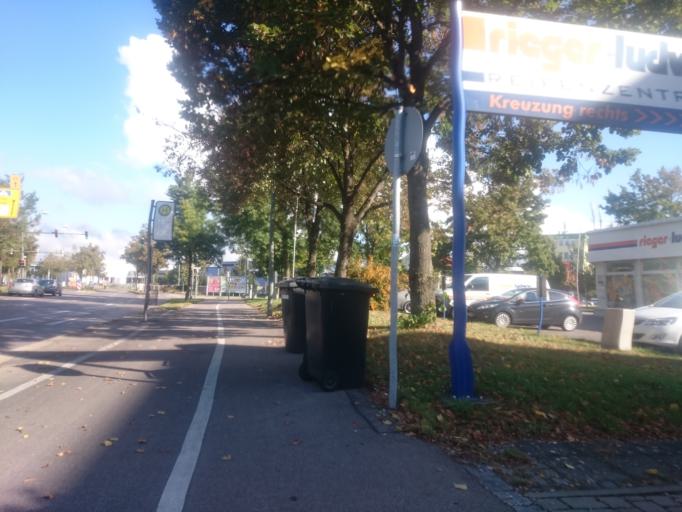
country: DE
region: Bavaria
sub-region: Swabia
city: Augsburg
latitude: 48.3767
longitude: 10.9292
